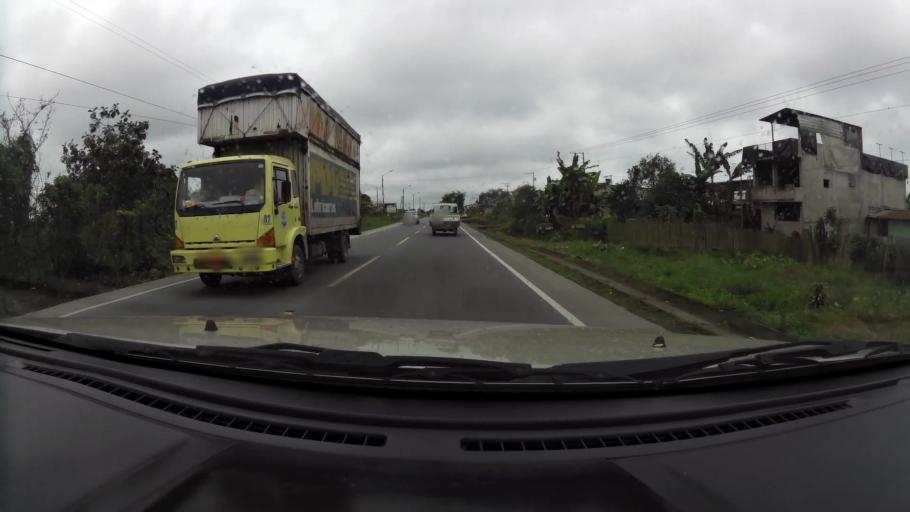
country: EC
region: Santo Domingo de los Tsachilas
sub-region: Canton Santo Domingo de los Colorados
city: Santo Domingo de los Colorados
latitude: -0.2767
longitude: -79.1707
